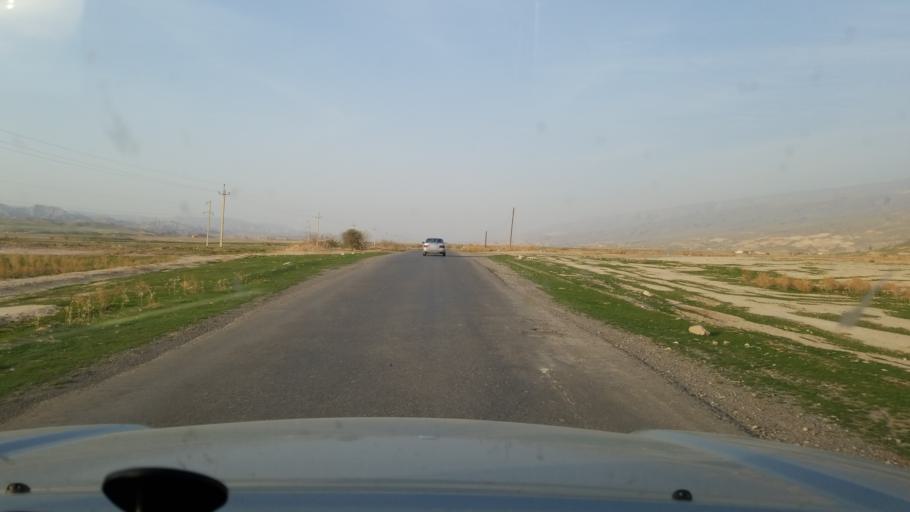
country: TM
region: Lebap
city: Gowurdak
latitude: 37.7488
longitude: 66.3501
